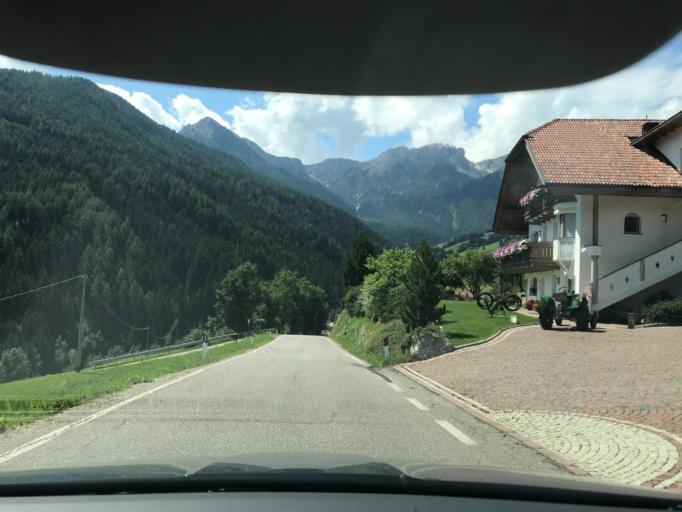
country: IT
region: Trentino-Alto Adige
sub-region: Bolzano
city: Valdaora di Mezzo
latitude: 46.7522
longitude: 12.0122
